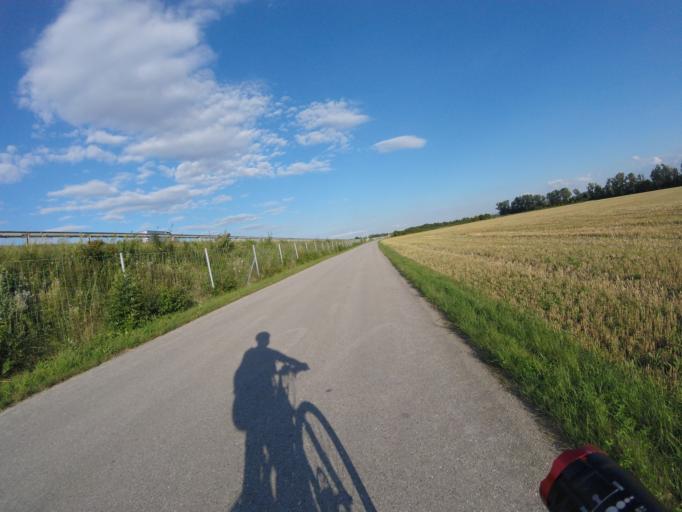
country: AT
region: Lower Austria
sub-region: Politischer Bezirk Baden
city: Trumau
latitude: 48.0257
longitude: 16.3481
